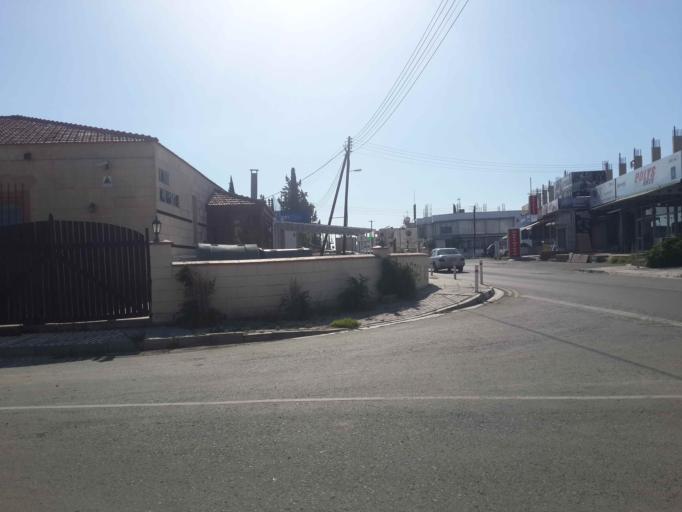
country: CY
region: Lefkosia
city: Nicosia
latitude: 35.1466
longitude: 33.3303
